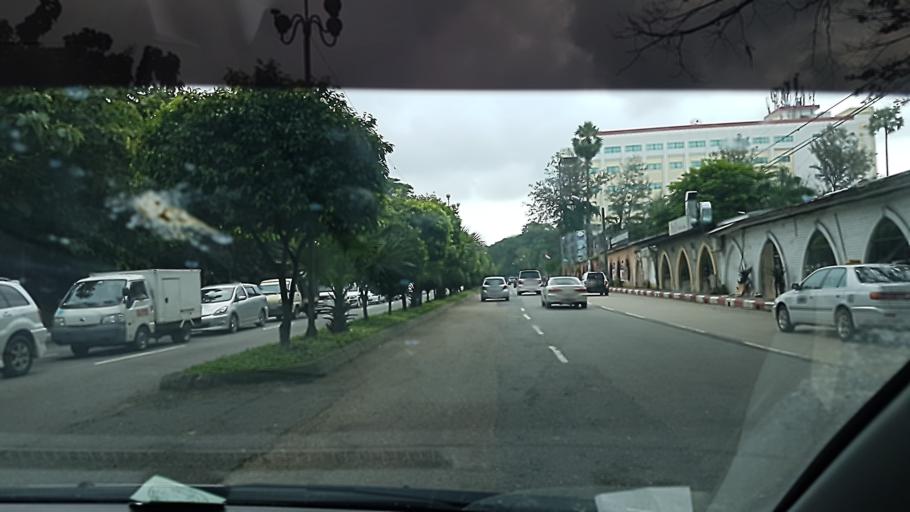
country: MM
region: Yangon
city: Yangon
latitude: 16.7932
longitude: 96.1412
